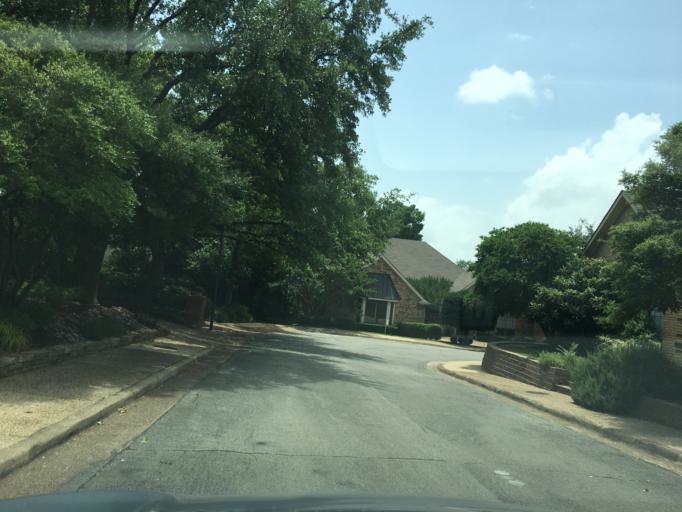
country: US
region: Texas
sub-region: Dallas County
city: University Park
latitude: 32.9108
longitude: -96.7904
